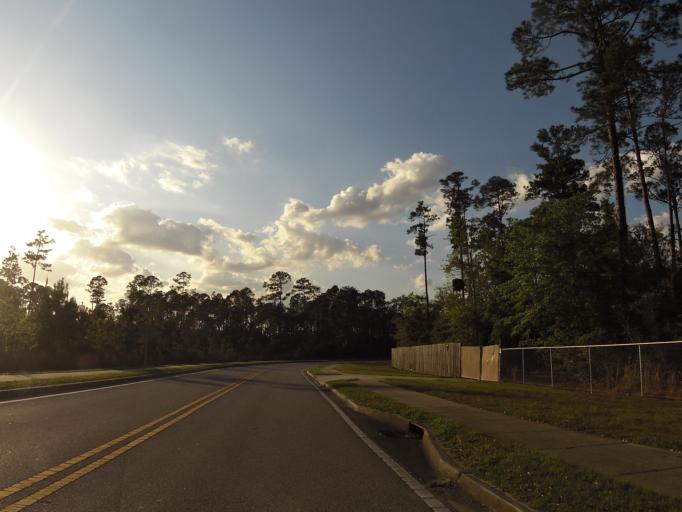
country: US
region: Florida
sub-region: Saint Johns County
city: Fruit Cove
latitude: 30.0649
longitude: -81.5061
